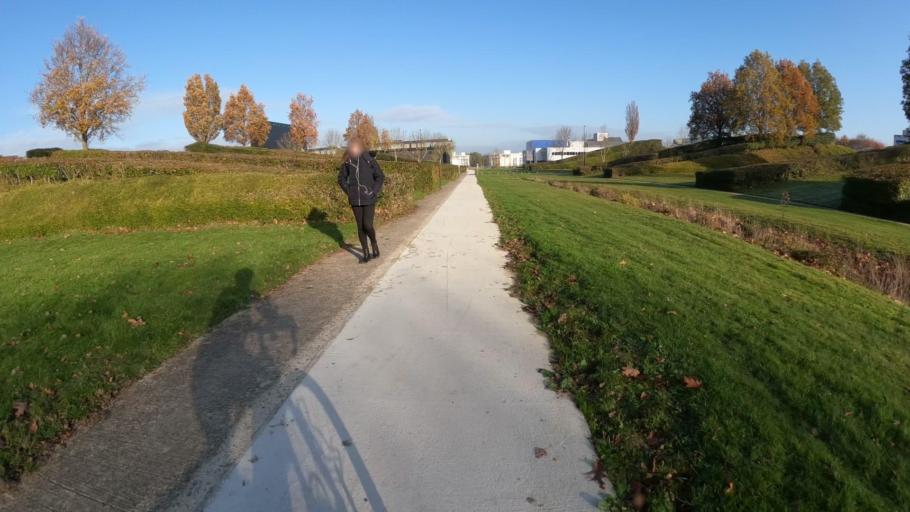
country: FR
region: Lower Normandy
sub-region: Departement du Calvados
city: Epron
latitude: 49.2137
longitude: -0.3546
